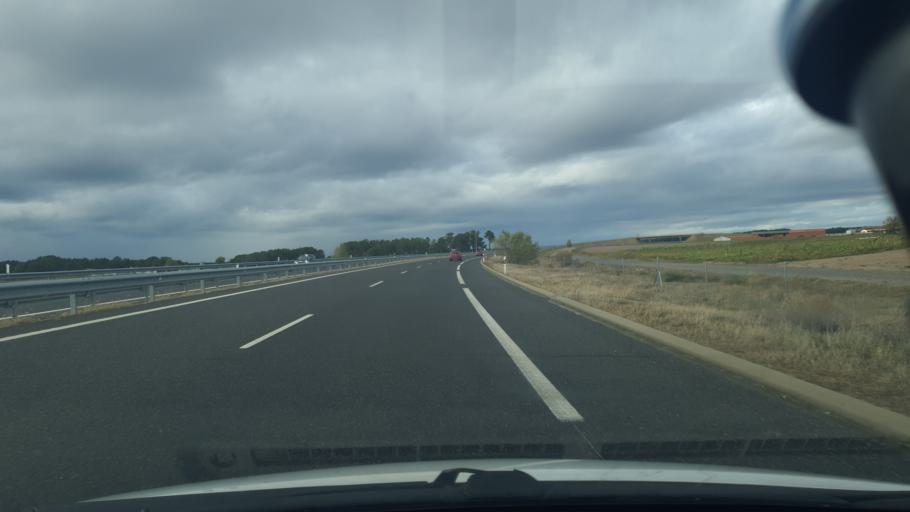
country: ES
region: Castille and Leon
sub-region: Provincia de Segovia
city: Pinarejos
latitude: 41.2536
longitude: -4.2956
